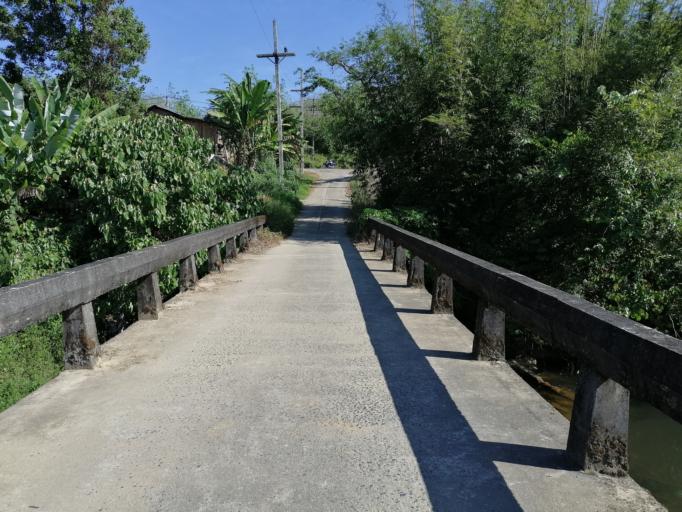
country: TH
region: Phangnga
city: Kapong
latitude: 8.5631
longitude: 98.4340
